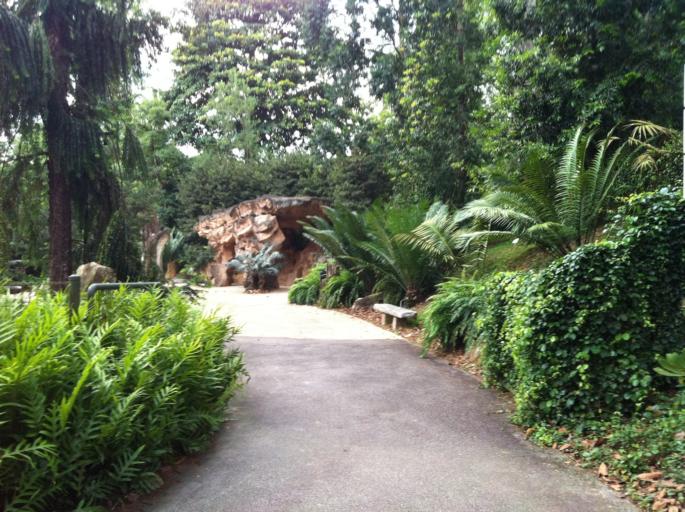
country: SG
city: Singapore
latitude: 1.3164
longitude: 103.8165
